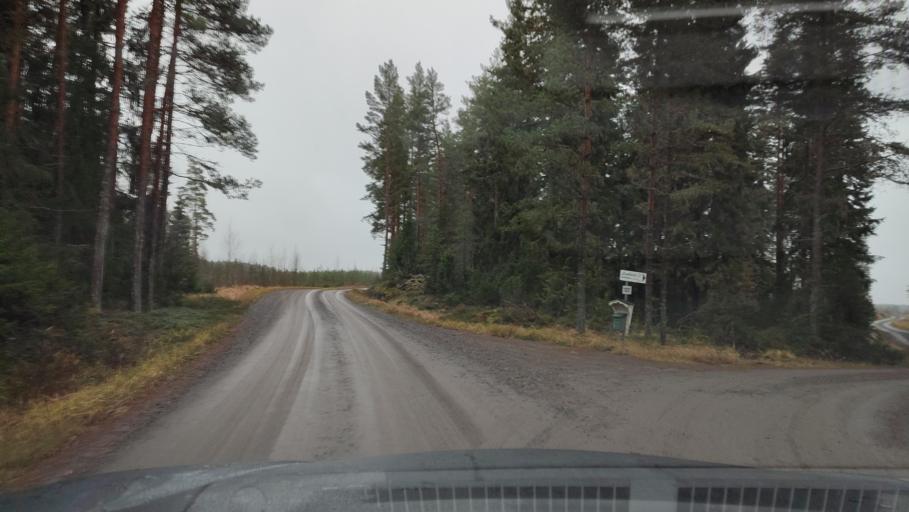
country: FI
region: Southern Ostrobothnia
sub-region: Suupohja
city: Karijoki
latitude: 62.2256
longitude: 21.5719
